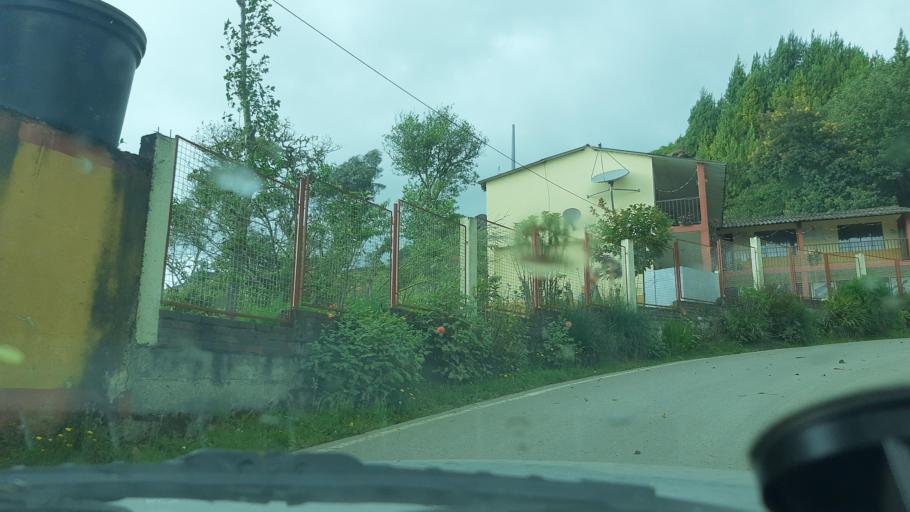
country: CO
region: Cundinamarca
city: Umbita
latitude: 5.2150
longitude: -73.4745
